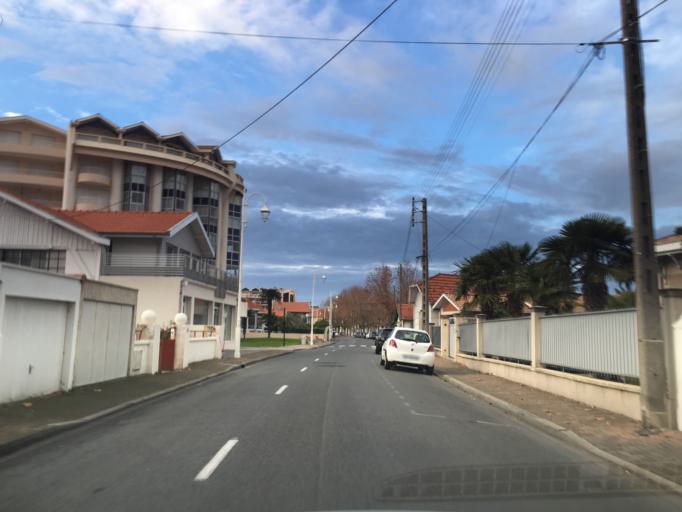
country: FR
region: Aquitaine
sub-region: Departement de la Gironde
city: Arcachon
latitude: 44.6586
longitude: -1.1512
